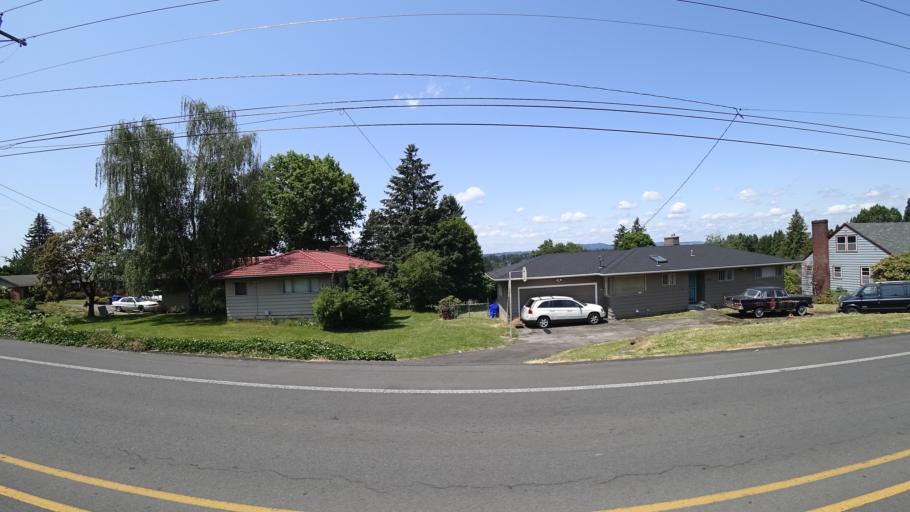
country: US
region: Oregon
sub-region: Multnomah County
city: Lents
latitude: 45.4589
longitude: -122.5687
